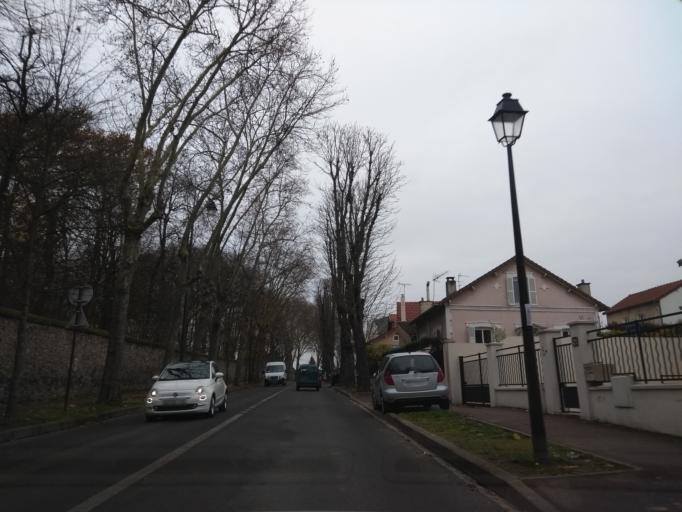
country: FR
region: Ile-de-France
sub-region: Departement des Hauts-de-Seine
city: Antony
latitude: 48.7575
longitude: 2.2933
